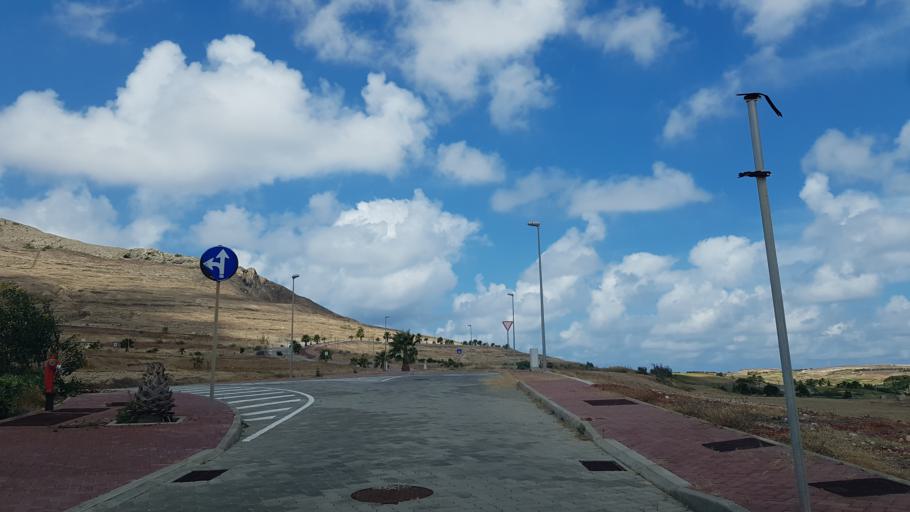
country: PT
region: Madeira
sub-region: Porto Santo
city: Vila de Porto Santo
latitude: 33.0499
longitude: -16.3627
